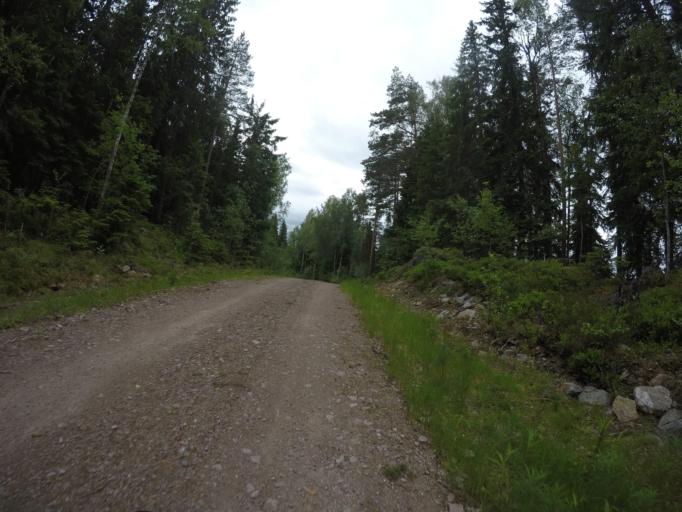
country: SE
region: Dalarna
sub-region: Ludvika Kommun
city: Abborrberget
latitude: 60.0702
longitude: 14.5639
